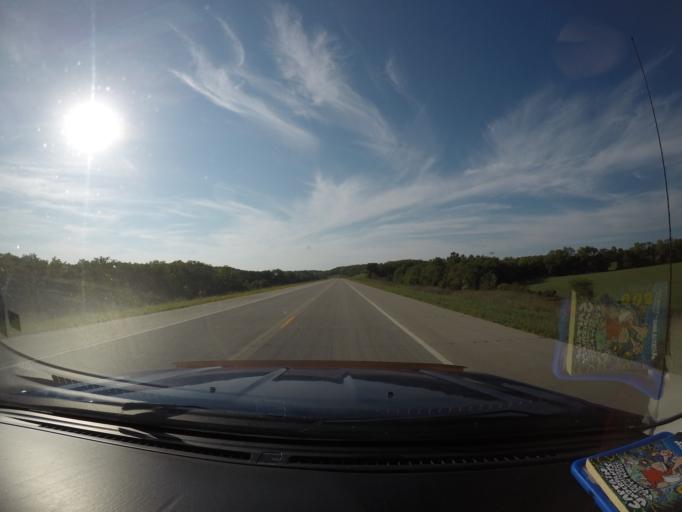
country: US
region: Kansas
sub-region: Leavenworth County
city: Leavenworth
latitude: 39.3562
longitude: -95.0084
